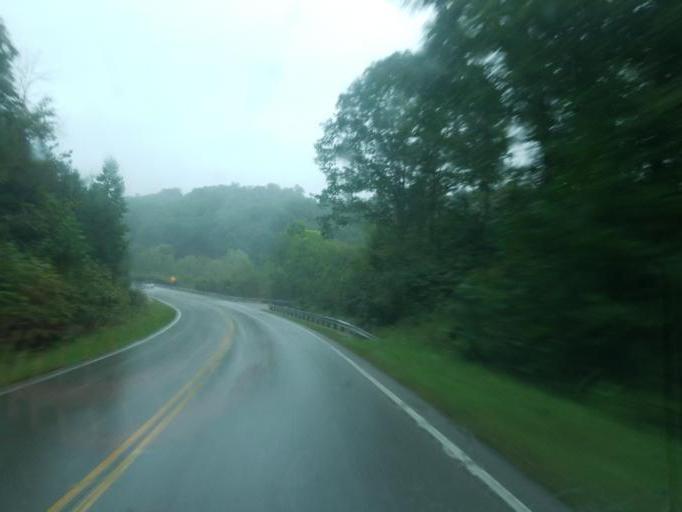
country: US
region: Kentucky
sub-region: Carter County
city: Olive Hill
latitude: 38.3351
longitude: -83.2038
